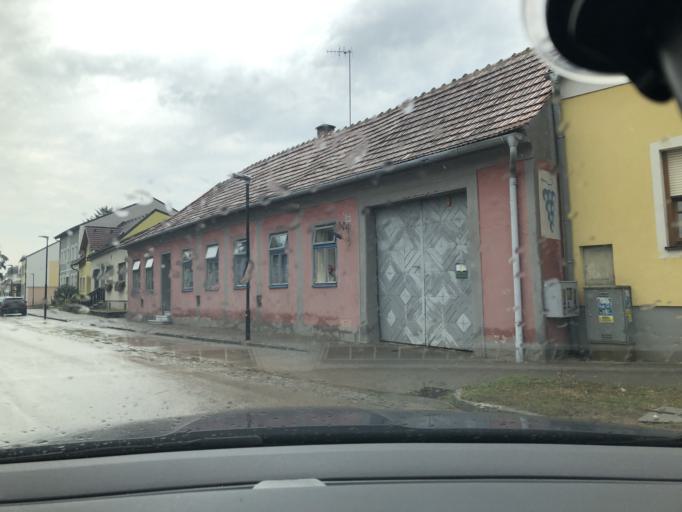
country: AT
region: Lower Austria
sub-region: Politischer Bezirk Ganserndorf
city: Auersthal
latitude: 48.3722
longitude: 16.6419
